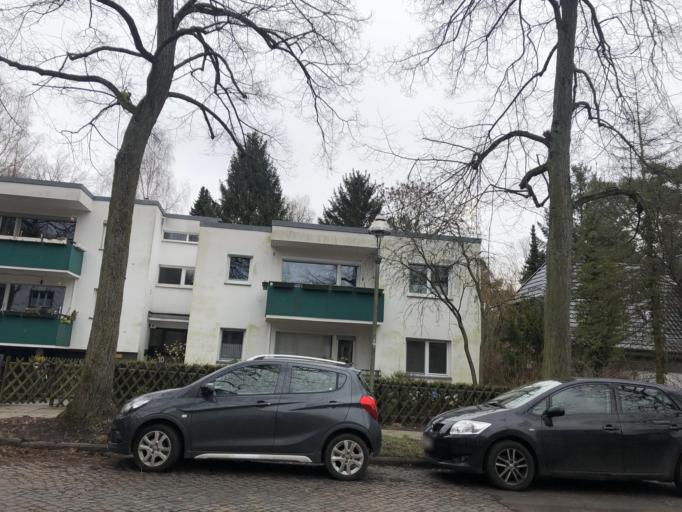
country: DE
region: Berlin
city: Frohnau
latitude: 52.6446
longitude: 13.3021
